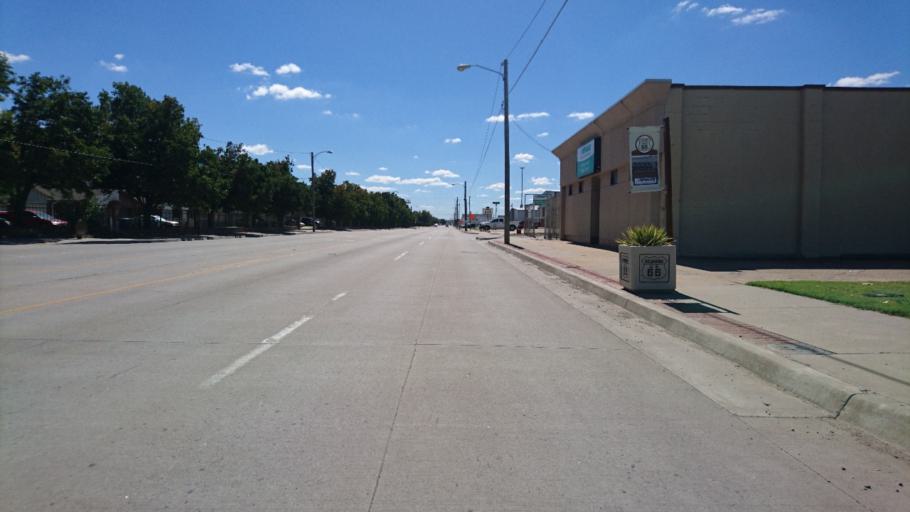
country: US
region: Oklahoma
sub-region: Tulsa County
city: Tulsa
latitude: 36.1359
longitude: -96.0071
